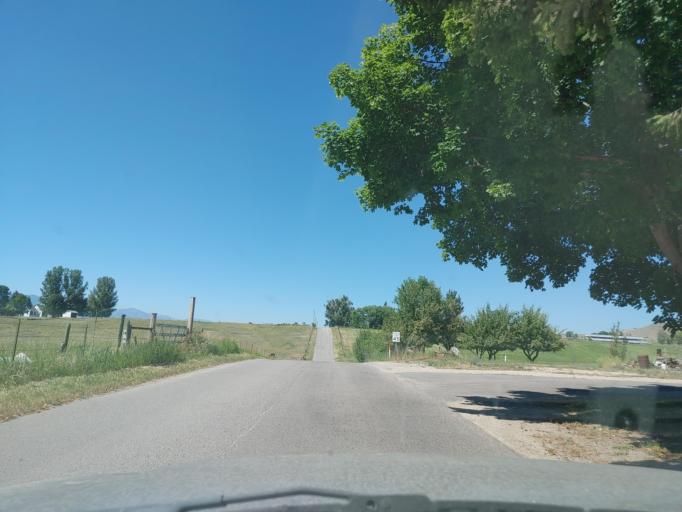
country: US
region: Montana
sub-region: Ravalli County
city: Hamilton
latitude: 46.3130
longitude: -114.0612
